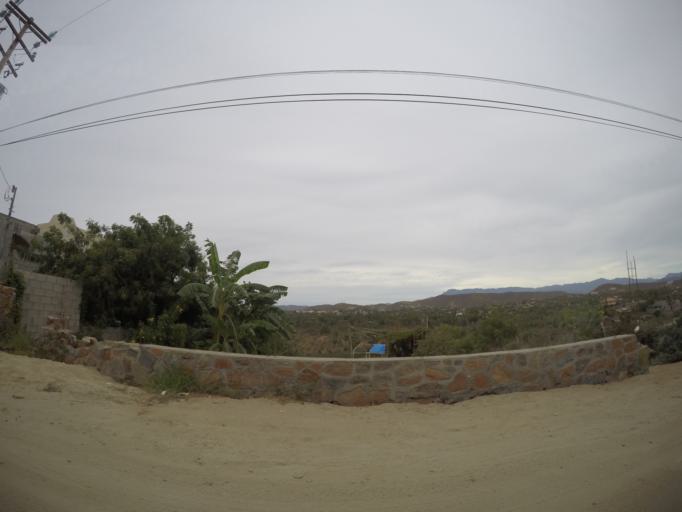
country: MX
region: Baja California Sur
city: Todos Santos
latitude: 23.4407
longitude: -110.2317
